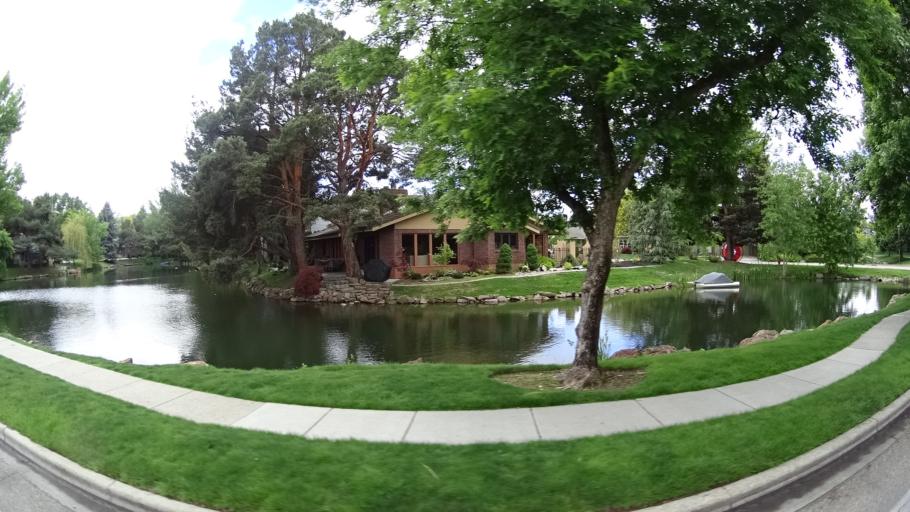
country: US
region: Idaho
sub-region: Ada County
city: Garden City
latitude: 43.6646
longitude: -116.2852
